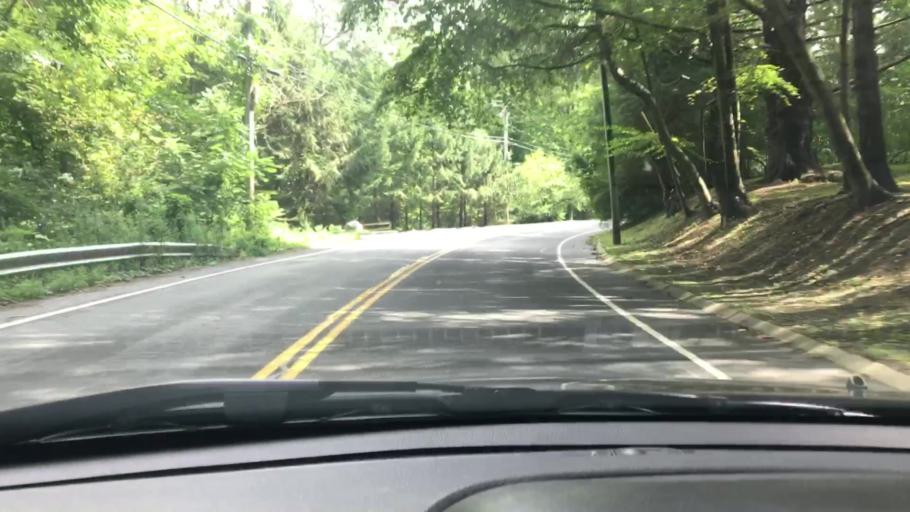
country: US
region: New York
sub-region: Westchester County
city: Bedford Hills
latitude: 41.2242
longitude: -73.6793
